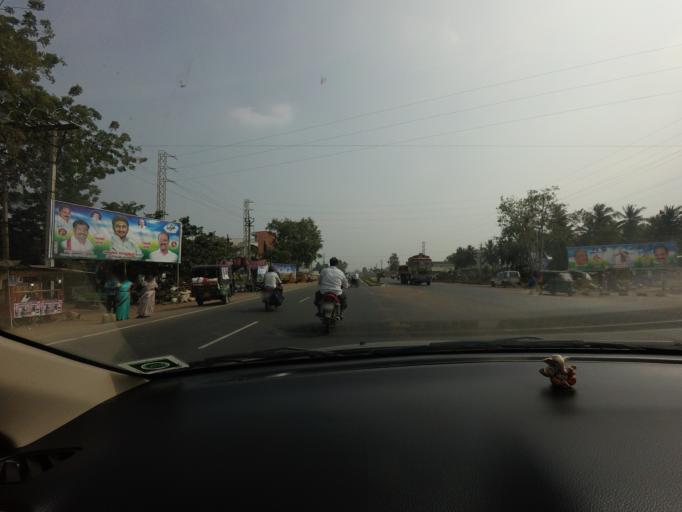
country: IN
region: Andhra Pradesh
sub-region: Krishna
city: Kankipadu
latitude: 16.4483
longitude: 80.7486
